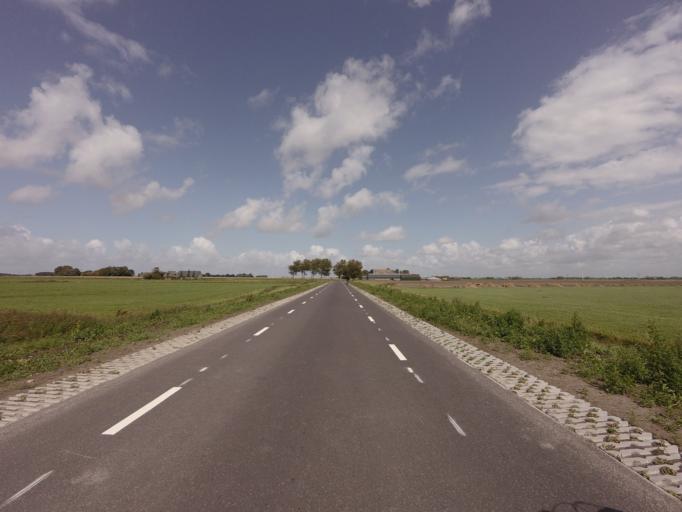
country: NL
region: Friesland
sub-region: Gemeente Harlingen
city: Harlingen
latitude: 53.1518
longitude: 5.4774
